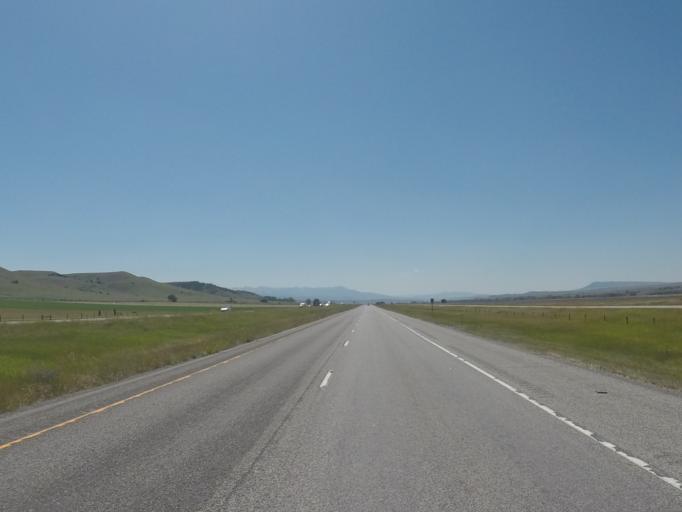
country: US
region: Montana
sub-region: Sweet Grass County
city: Big Timber
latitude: 45.8111
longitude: -110.0083
